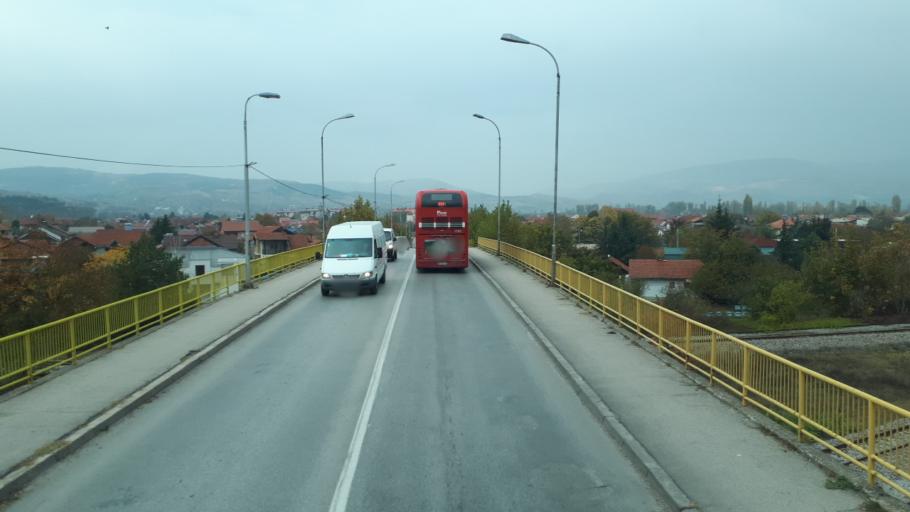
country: MK
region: Saraj
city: Saraj
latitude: 42.0127
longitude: 21.3596
